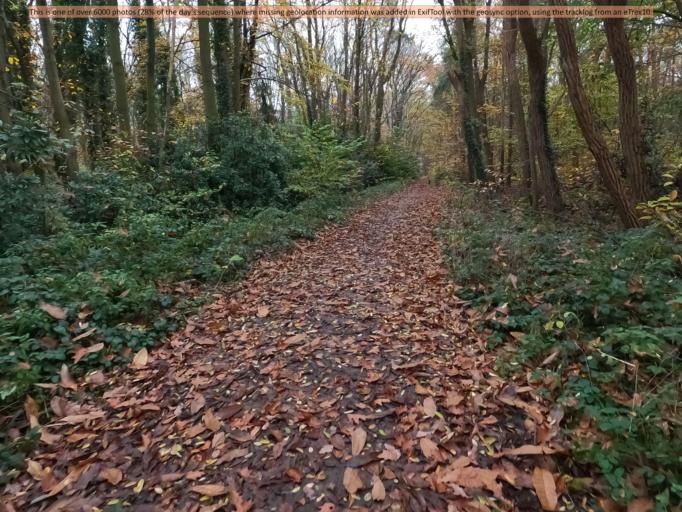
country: BE
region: Flanders
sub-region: Provincie Antwerpen
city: Nijlen
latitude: 51.1329
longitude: 4.7085
